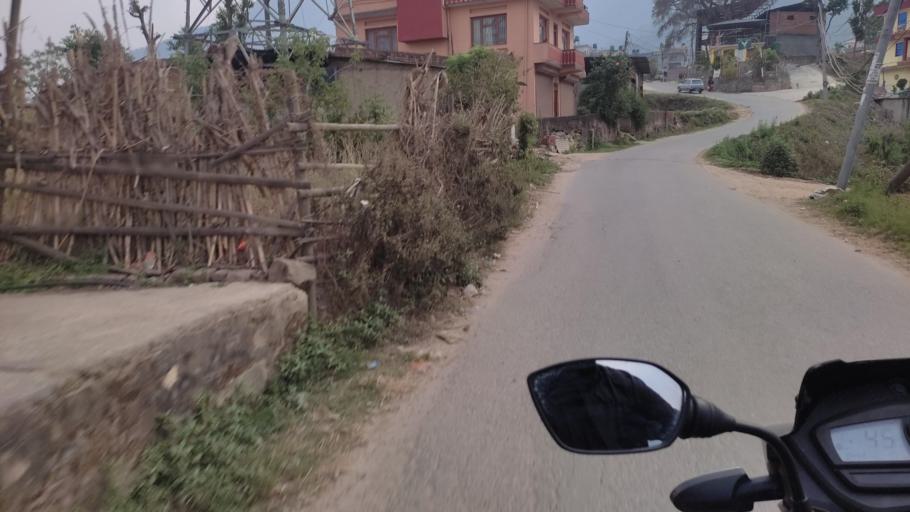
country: NP
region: Central Region
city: Kirtipur
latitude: 27.6777
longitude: 85.2543
